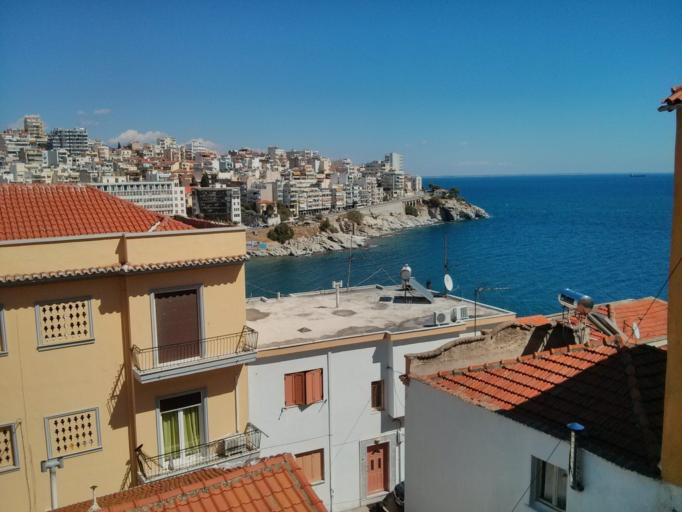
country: GR
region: East Macedonia and Thrace
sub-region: Nomos Kavalas
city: Kavala
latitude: 40.9353
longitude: 24.4170
